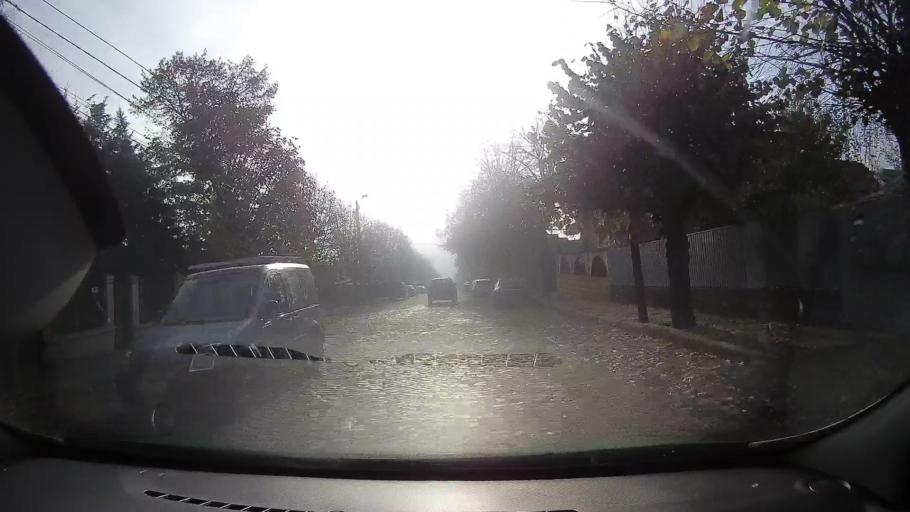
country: RO
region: Tulcea
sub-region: Municipiul Tulcea
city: Tulcea
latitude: 45.1679
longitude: 28.8146
